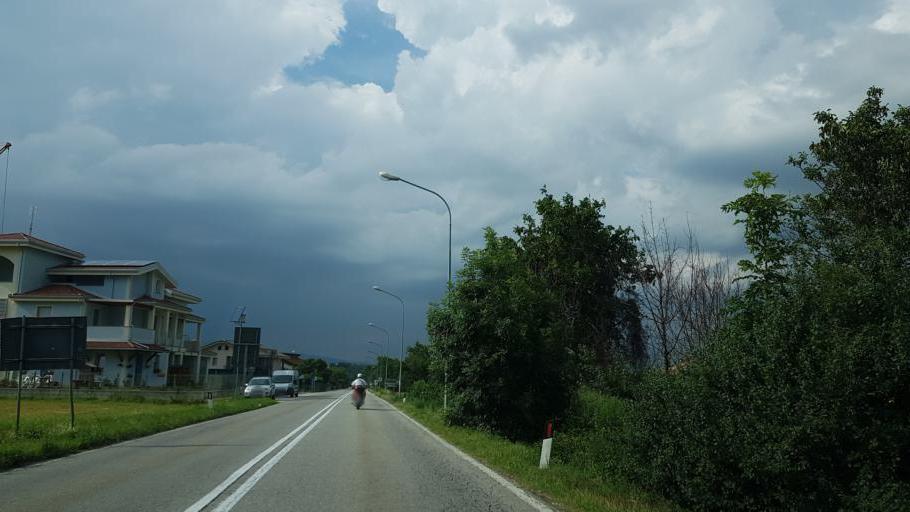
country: IT
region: Piedmont
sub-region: Provincia di Cuneo
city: Vignolo
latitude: 44.3563
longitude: 7.4784
